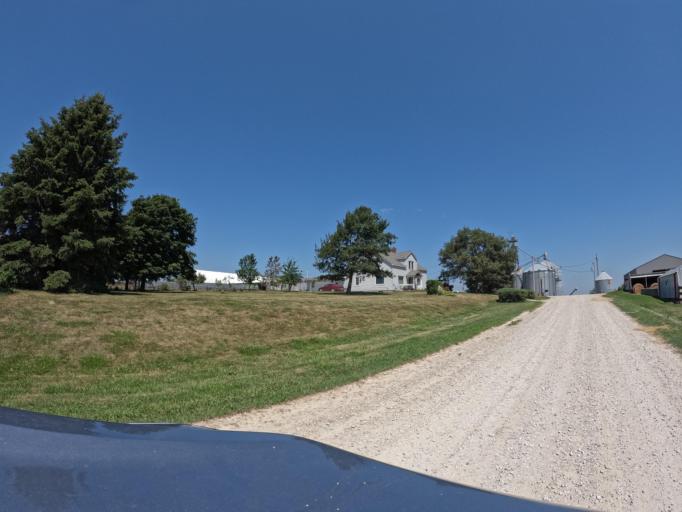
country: US
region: Iowa
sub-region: Keokuk County
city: Sigourney
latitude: 41.2698
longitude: -92.2190
